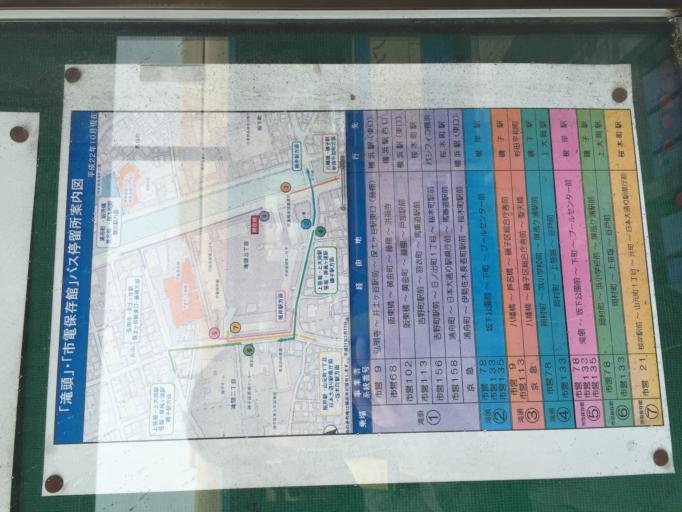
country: JP
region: Kanagawa
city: Yokohama
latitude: 35.4198
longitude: 139.6255
